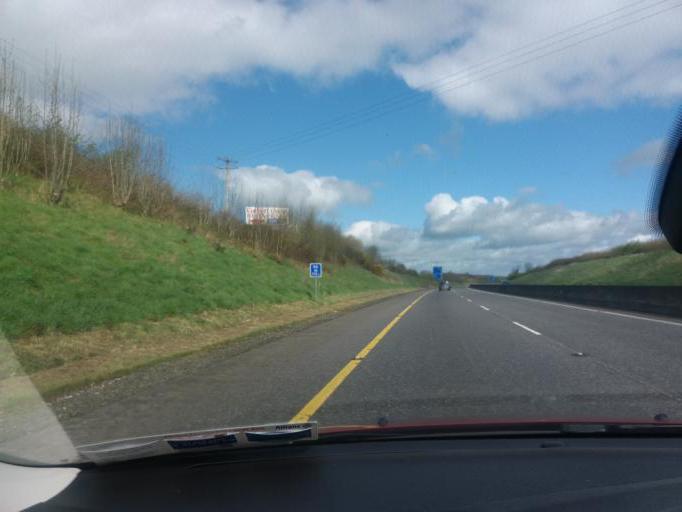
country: IE
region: Munster
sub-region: County Cork
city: Fermoy
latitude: 52.1458
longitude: -8.2653
